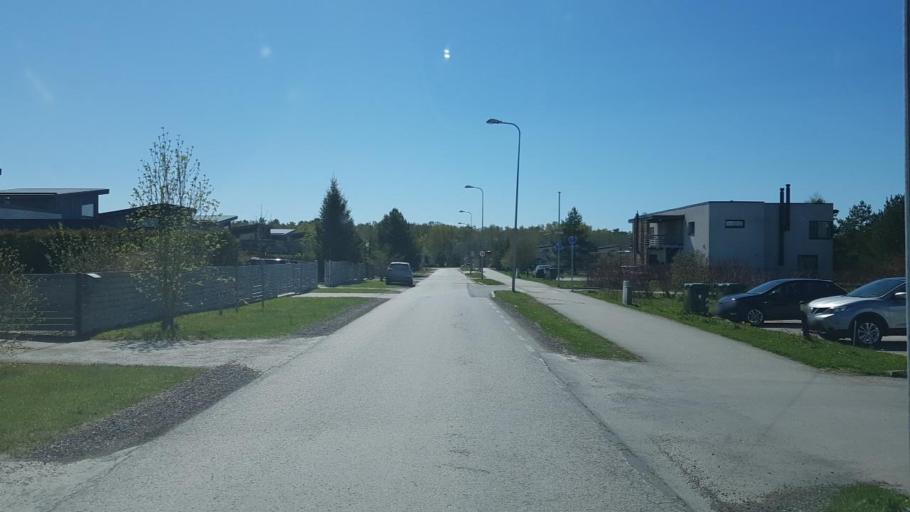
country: EE
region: Harju
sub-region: Viimsi vald
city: Viimsi
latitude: 59.5020
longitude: 24.8586
